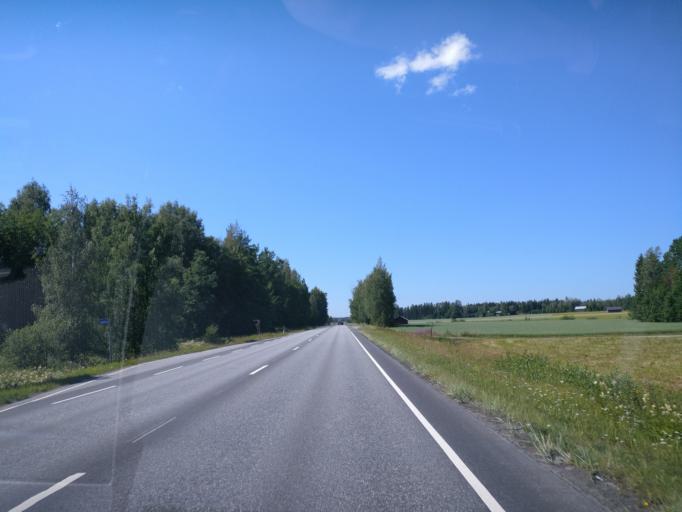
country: FI
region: Satakunta
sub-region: Pori
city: Nakkila
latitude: 61.4584
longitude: 22.0286
